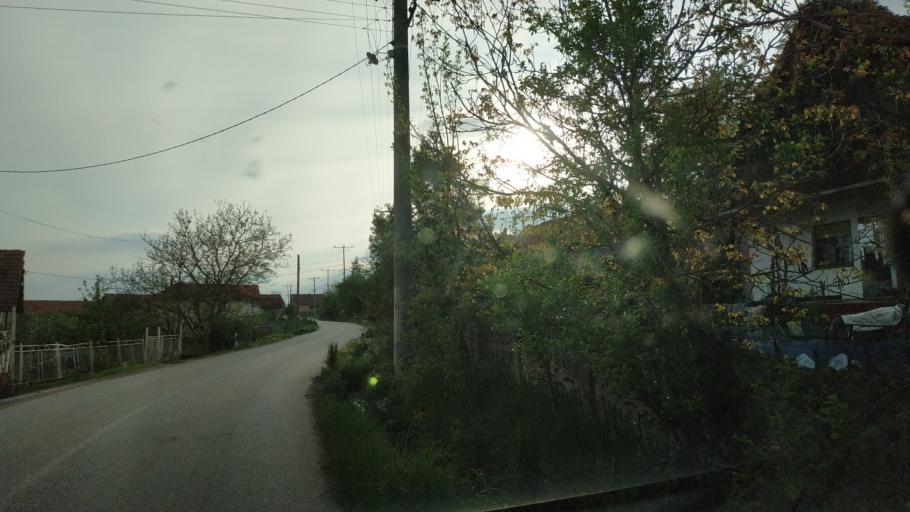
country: RS
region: Central Serbia
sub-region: Nisavski Okrug
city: Aleksinac
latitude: 43.4989
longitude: 21.8299
